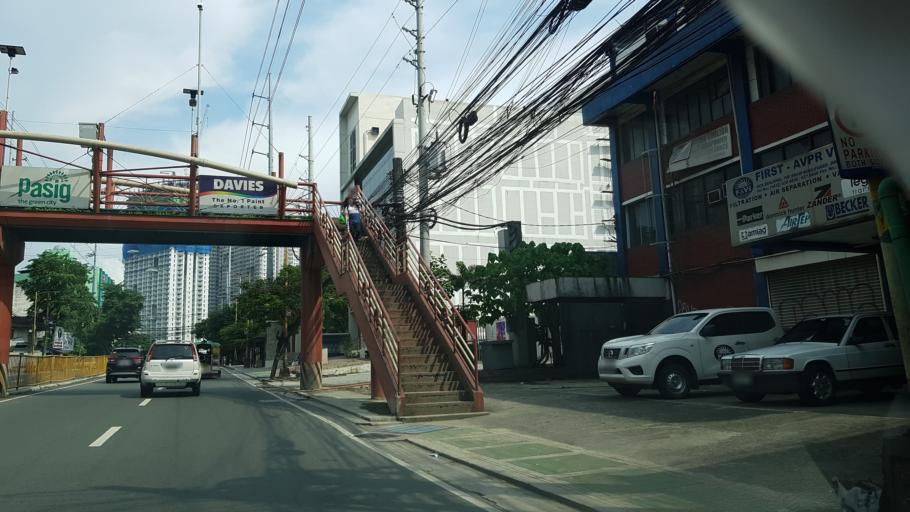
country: PH
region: Metro Manila
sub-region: Pasig
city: Pasig City
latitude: 14.5728
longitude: 121.0634
